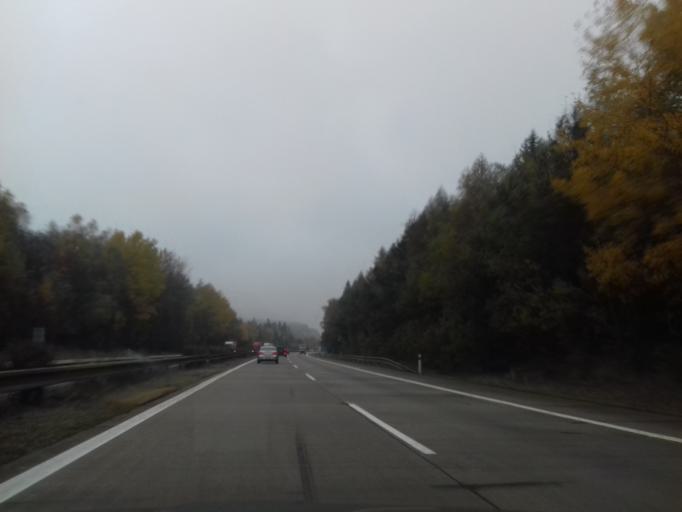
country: CZ
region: Vysocina
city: Heralec
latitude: 49.4947
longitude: 15.4859
